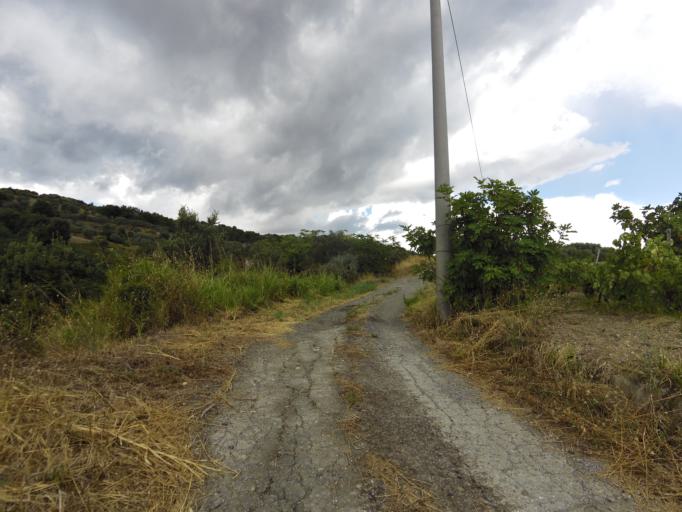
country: IT
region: Calabria
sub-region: Provincia di Reggio Calabria
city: Pazzano
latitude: 38.4446
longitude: 16.4529
